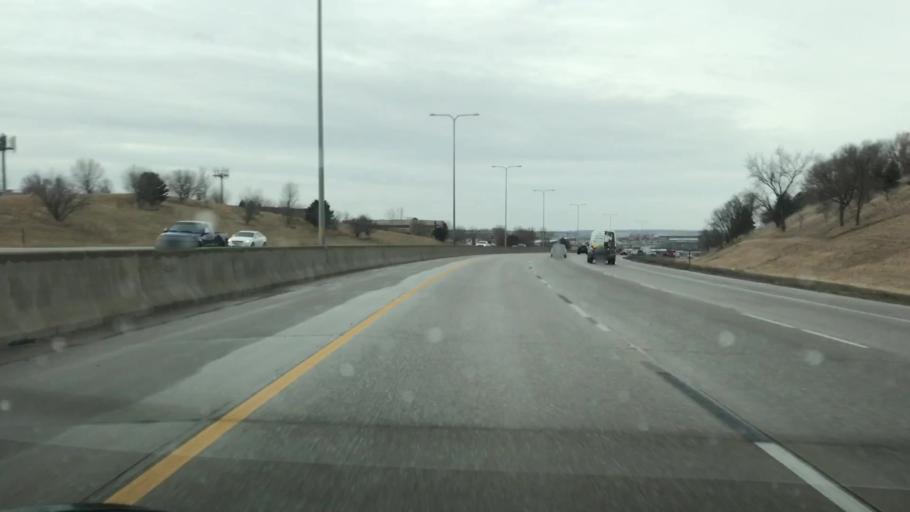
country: US
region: Nebraska
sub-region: Douglas County
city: Ralston
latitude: 41.1966
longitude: -96.0958
